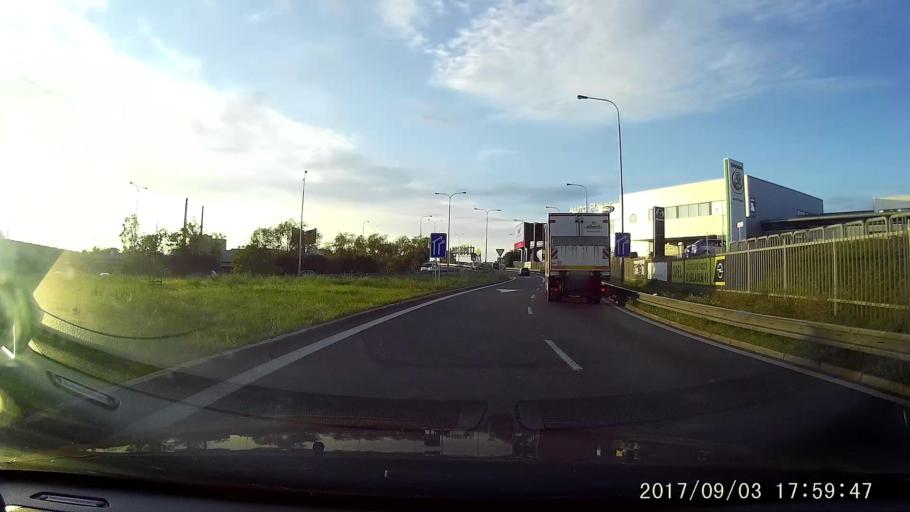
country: CZ
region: Praha
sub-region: Praha 8
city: Karlin
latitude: 50.0498
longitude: 14.4803
